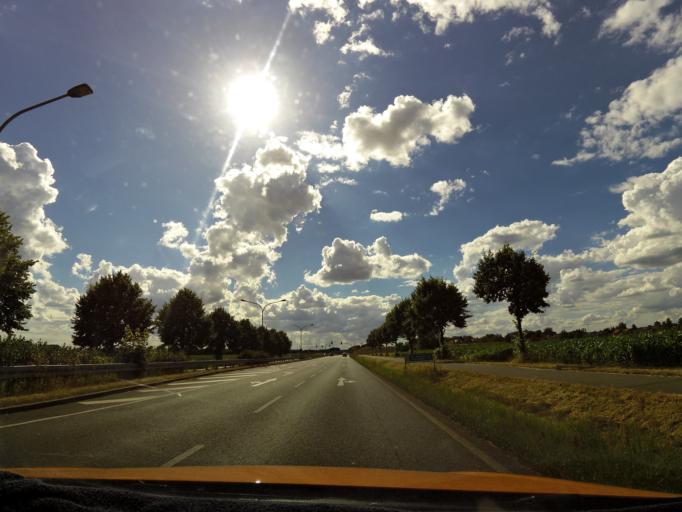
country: DE
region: Berlin
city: Lichtenrade
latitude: 52.3675
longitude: 13.3994
